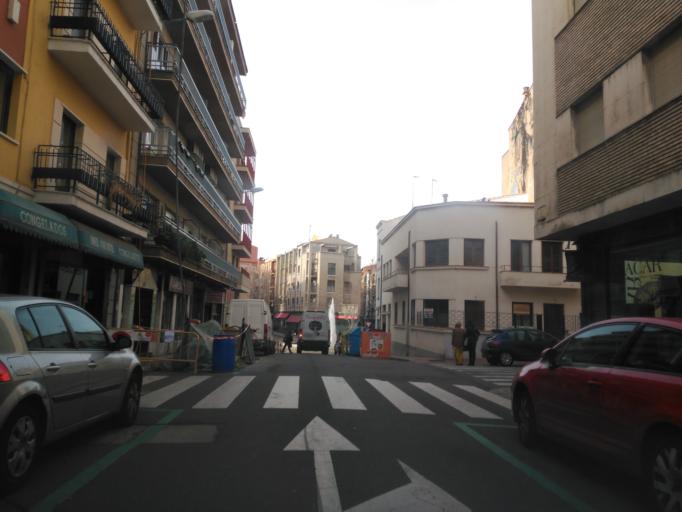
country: ES
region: Castille and Leon
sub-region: Provincia de Salamanca
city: Salamanca
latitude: 40.9704
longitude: -5.6667
